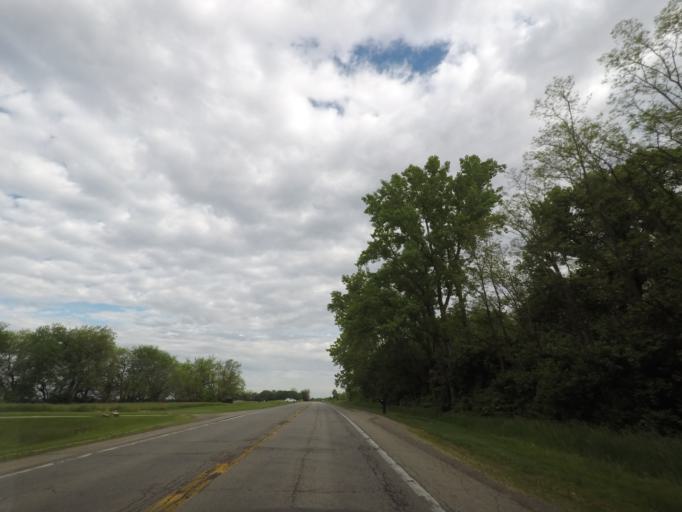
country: US
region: Illinois
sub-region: Logan County
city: Lincoln
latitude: 40.1234
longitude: -89.3382
